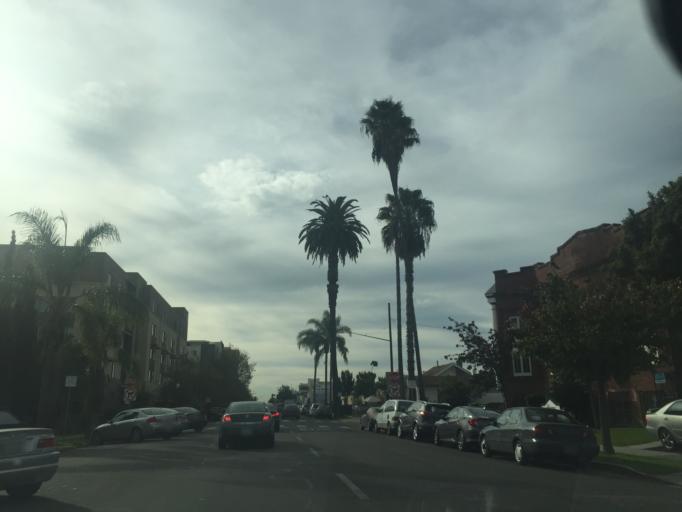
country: US
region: California
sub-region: San Diego County
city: San Diego
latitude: 32.7520
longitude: -117.1020
